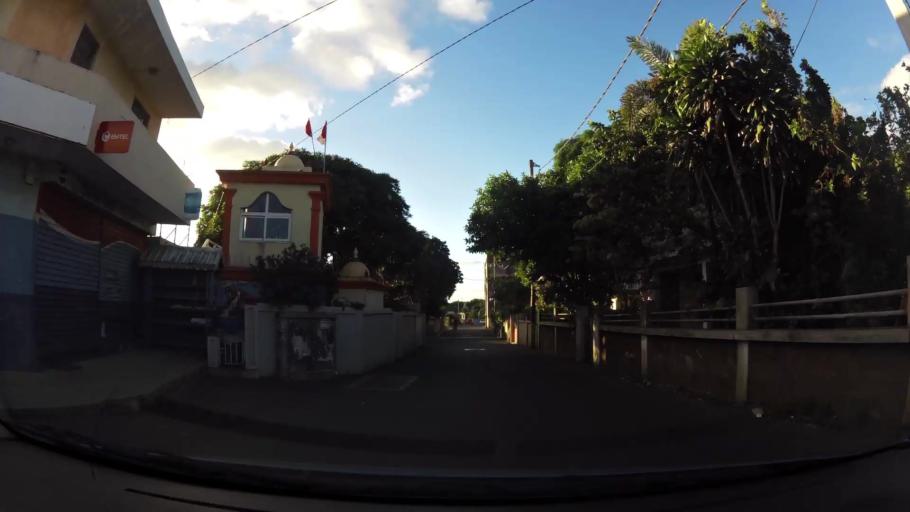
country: MU
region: Plaines Wilhems
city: Quatre Bornes
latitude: -20.2462
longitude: 57.4618
